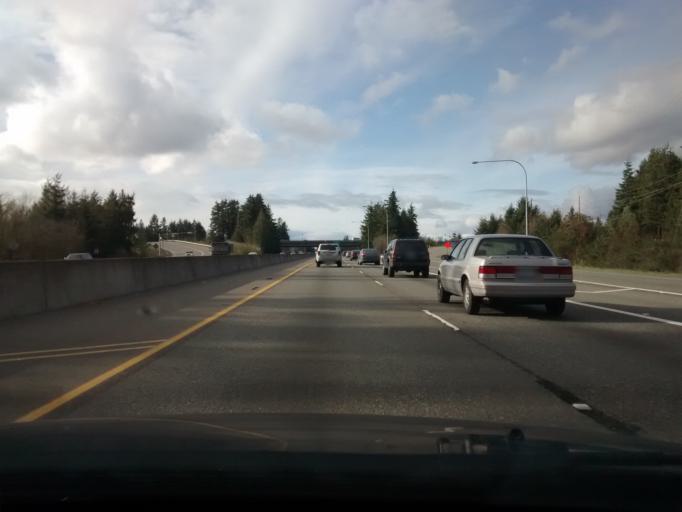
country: US
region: Washington
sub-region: Pierce County
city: Gig Harbor
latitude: 47.3022
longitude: -122.5736
